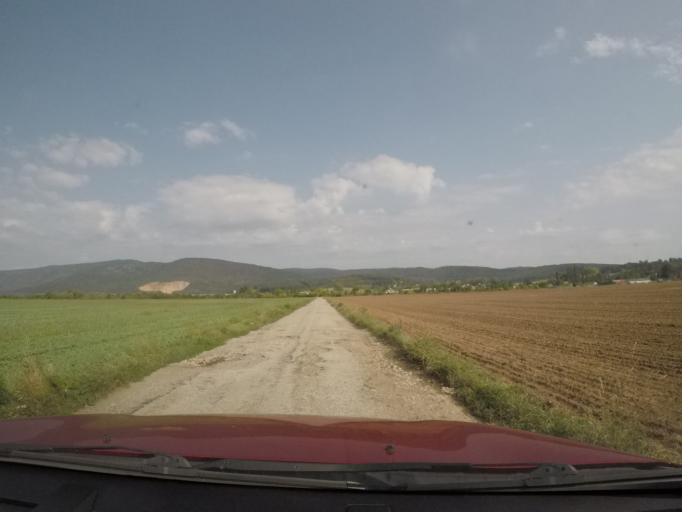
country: SK
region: Kosicky
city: Moldava nad Bodvou
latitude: 48.6017
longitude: 20.9534
